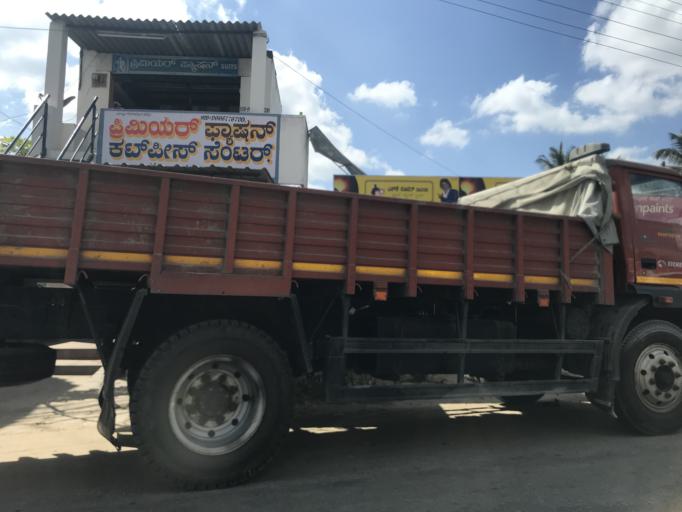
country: IN
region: Karnataka
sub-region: Hassan
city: Shravanabelagola
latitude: 12.7634
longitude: 76.4252
